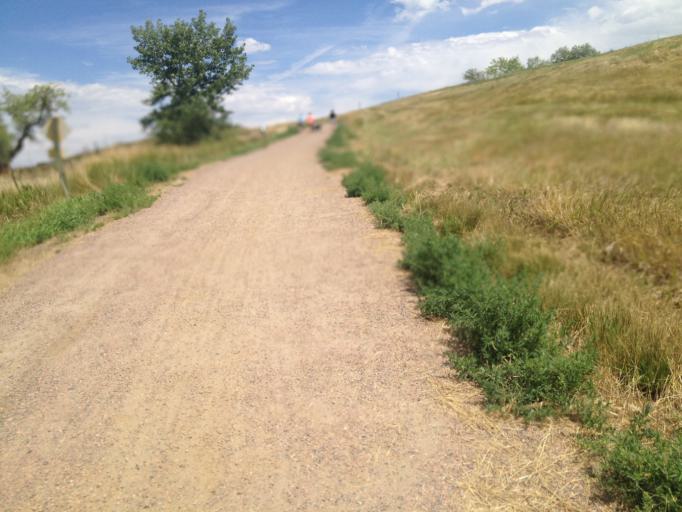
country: US
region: Colorado
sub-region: Boulder County
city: Louisville
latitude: 39.9728
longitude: -105.1208
